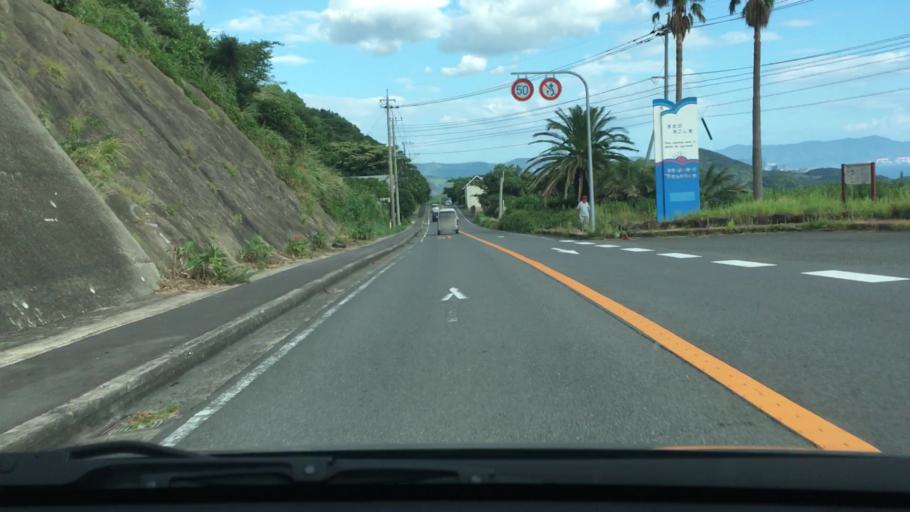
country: JP
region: Nagasaki
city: Togitsu
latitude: 32.8230
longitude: 129.7243
